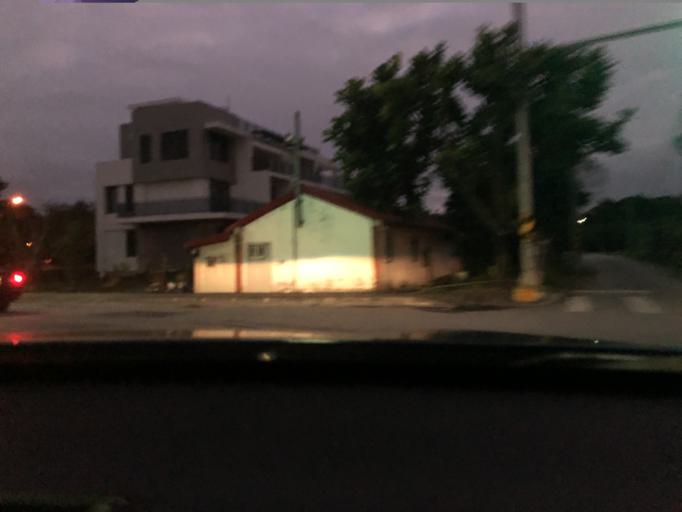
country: TW
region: Taiwan
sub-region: Hualien
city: Hualian
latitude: 23.9525
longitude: 121.5591
